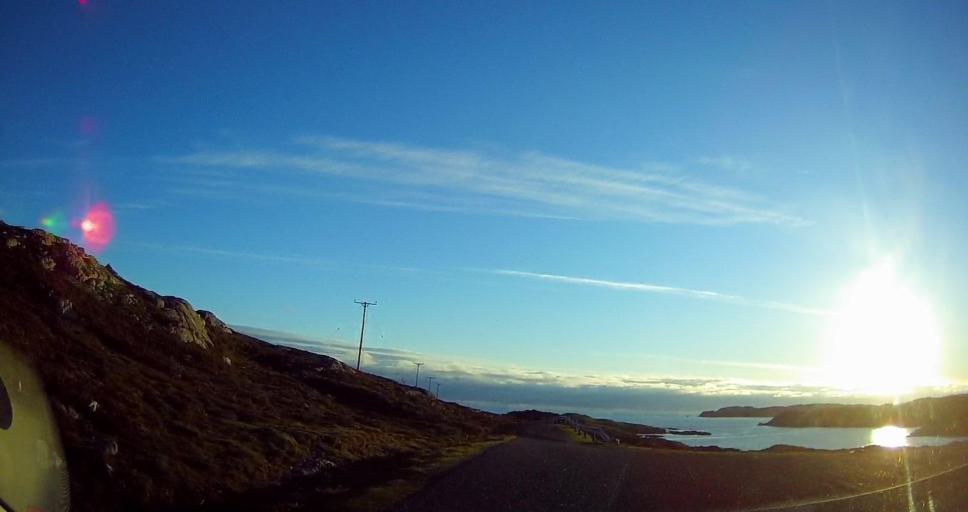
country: GB
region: Scotland
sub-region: Shetland Islands
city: Lerwick
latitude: 60.4453
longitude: -1.4352
